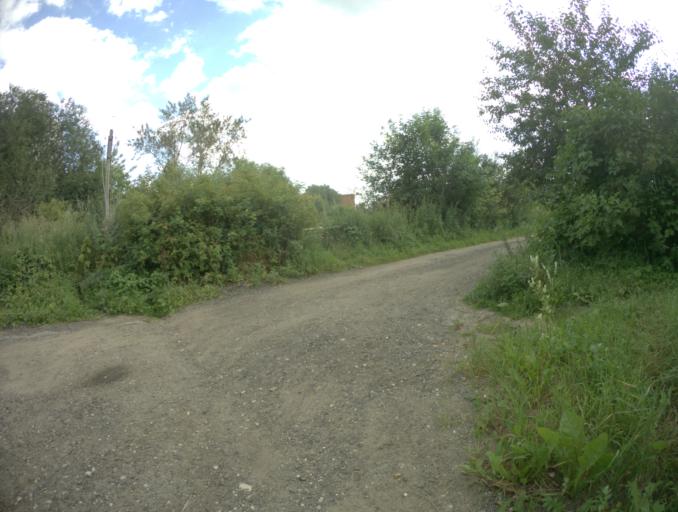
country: RU
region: Vladimir
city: Vladimir
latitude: 56.1132
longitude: 40.3718
